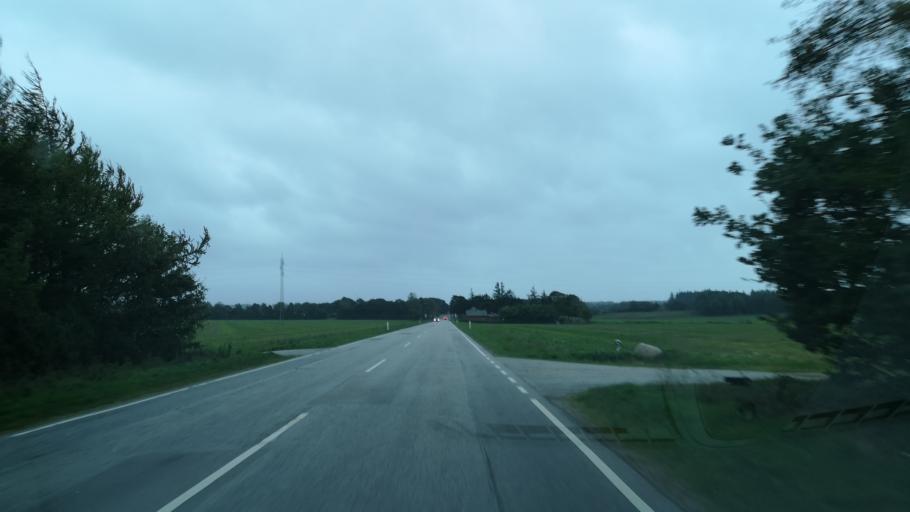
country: DK
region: Central Jutland
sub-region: Ringkobing-Skjern Kommune
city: Videbaek
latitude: 56.0511
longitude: 8.6247
